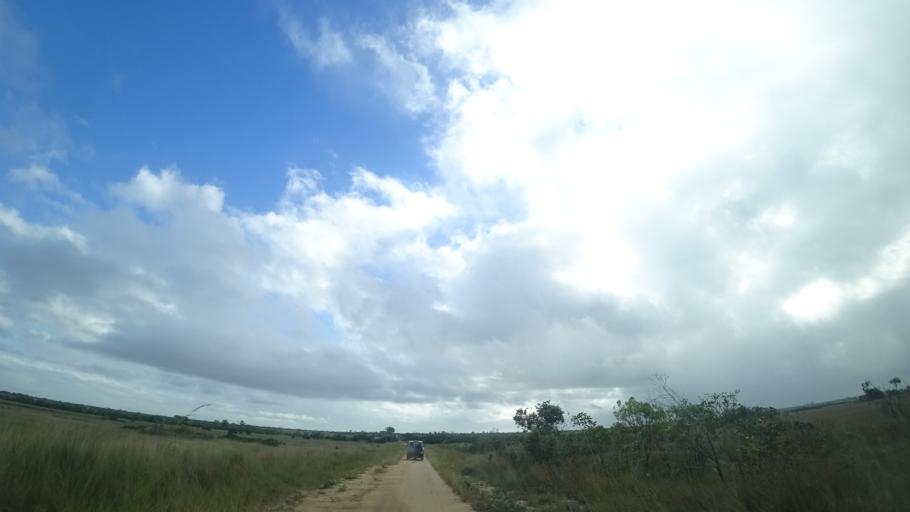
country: MZ
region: Sofala
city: Beira
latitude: -19.6329
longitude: 35.0598
